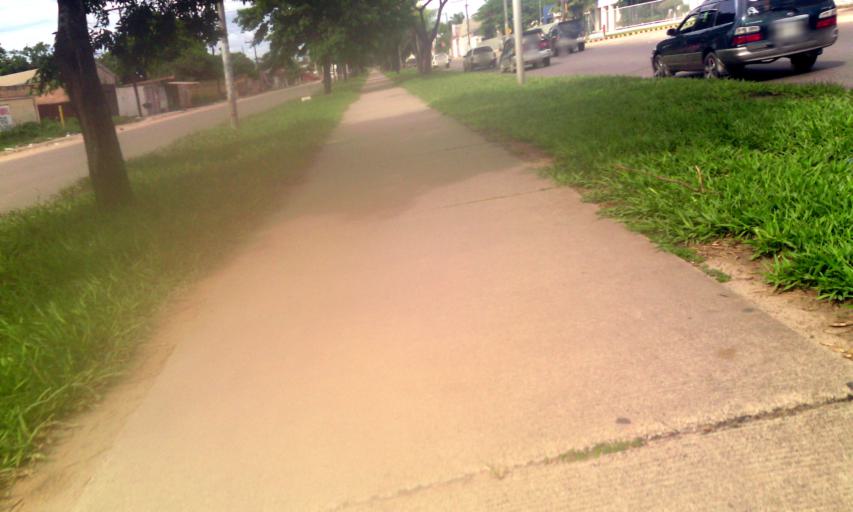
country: BO
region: Santa Cruz
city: Santa Cruz de la Sierra
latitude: -17.8410
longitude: -63.2413
